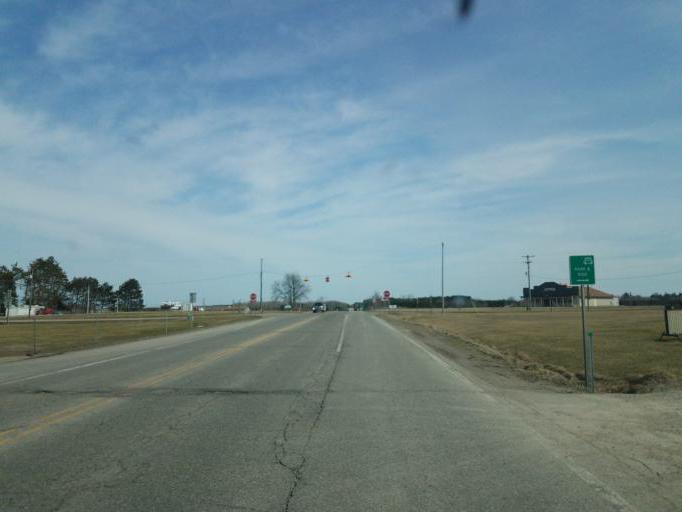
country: US
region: Michigan
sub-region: Osceola County
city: Evart
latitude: 43.9006
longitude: -85.1488
